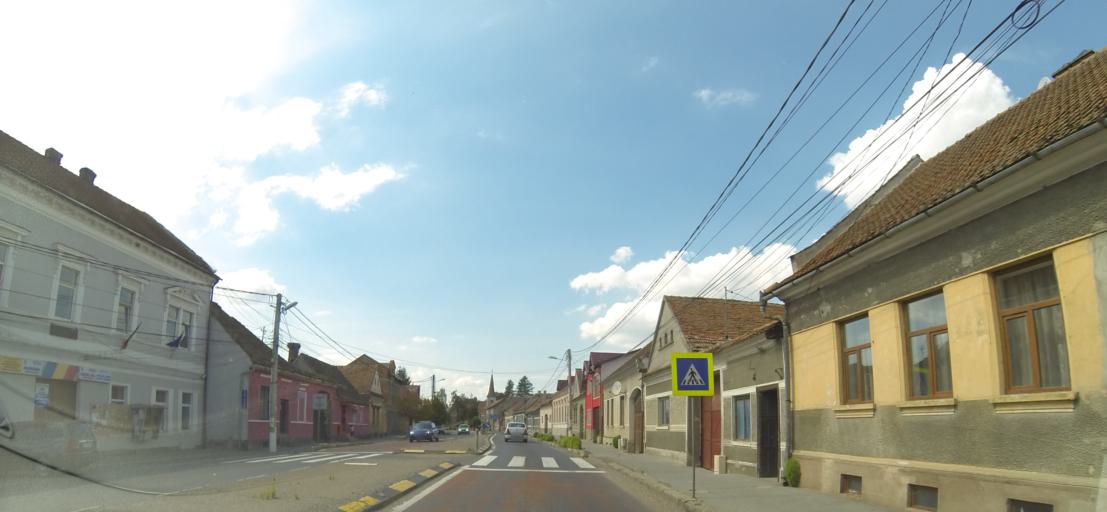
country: RO
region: Brasov
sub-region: Comuna Sercaia
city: Sercaia
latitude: 45.8306
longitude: 25.1408
